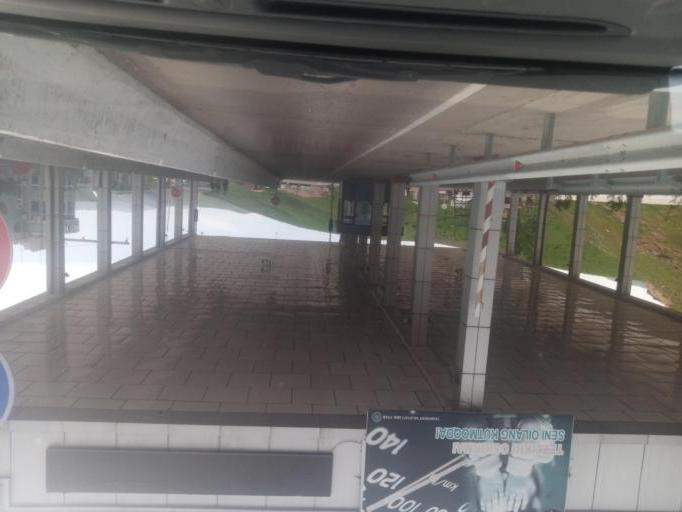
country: UZ
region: Toshkent
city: Angren
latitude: 41.0640
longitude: 70.2146
